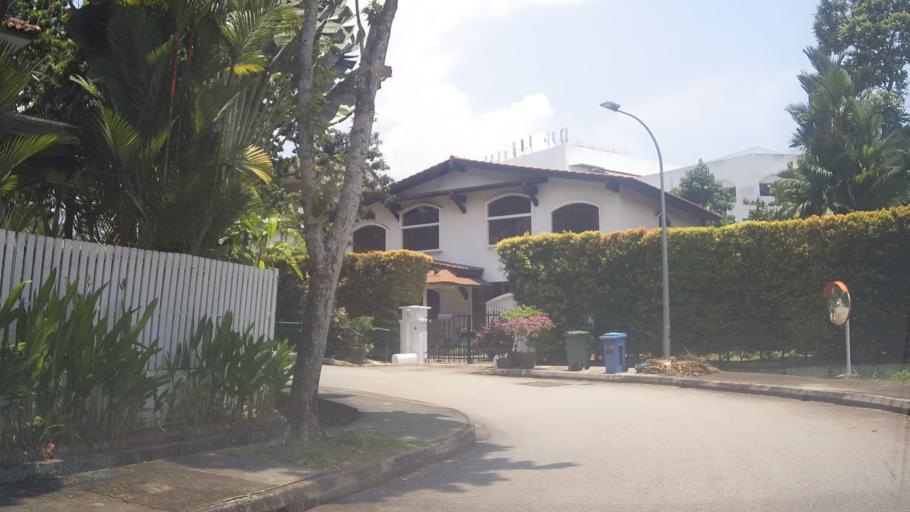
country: SG
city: Singapore
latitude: 1.3377
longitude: 103.7833
